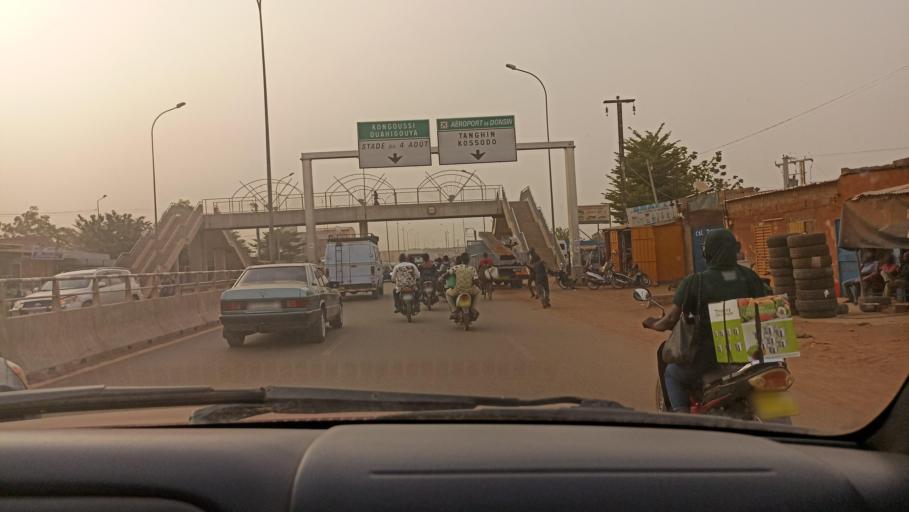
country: BF
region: Centre
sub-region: Kadiogo Province
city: Ouagadougou
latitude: 12.3815
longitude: -1.5508
